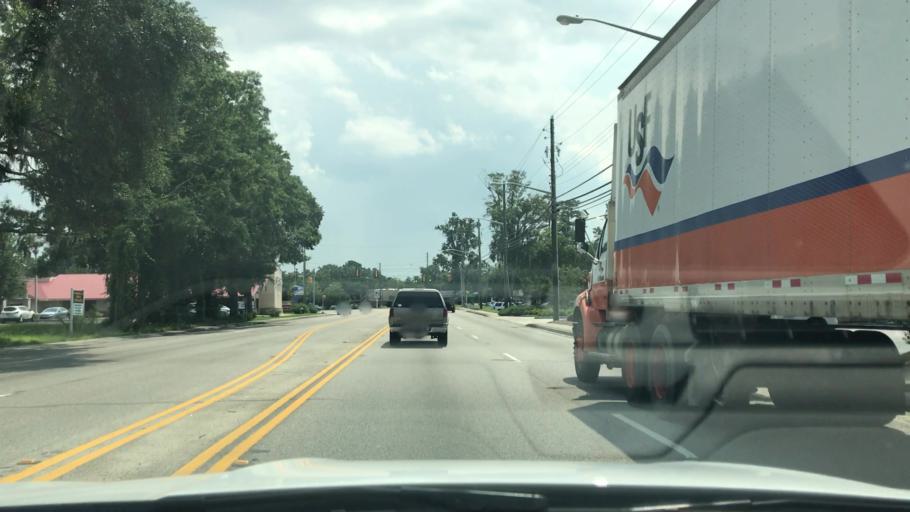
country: US
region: South Carolina
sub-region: Georgetown County
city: Georgetown
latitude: 33.3891
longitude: -79.2891
